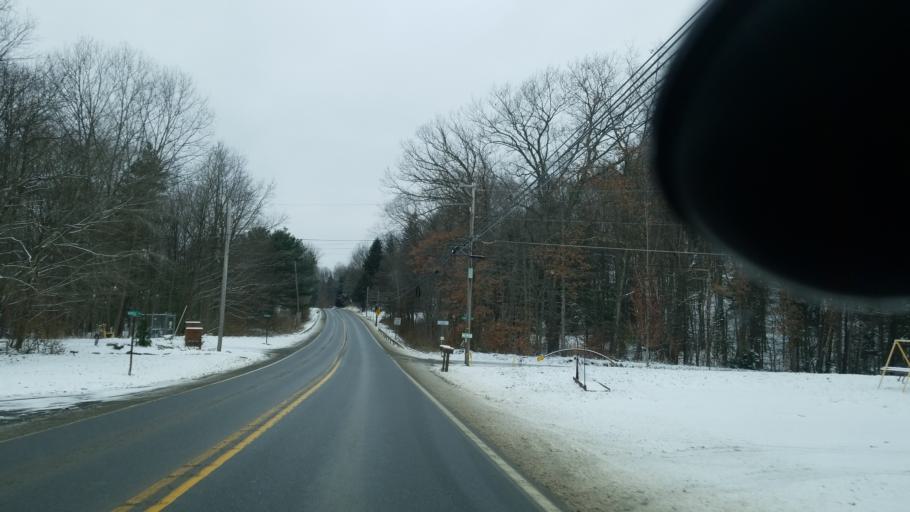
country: US
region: Pennsylvania
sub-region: Jefferson County
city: Albion
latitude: 40.9377
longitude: -78.9229
